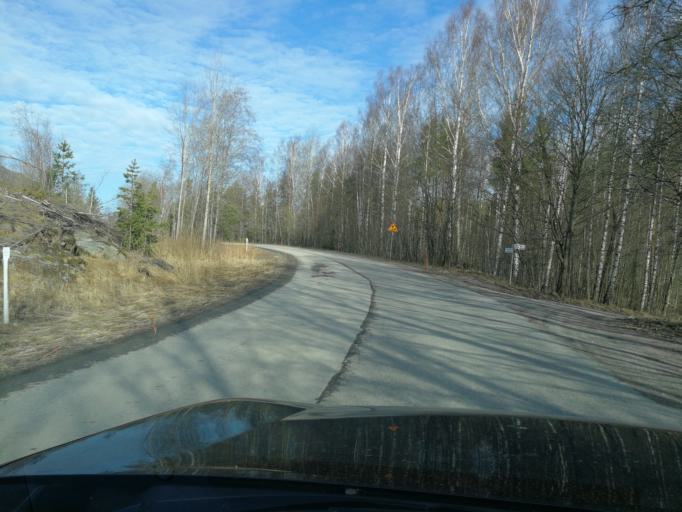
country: FI
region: Uusimaa
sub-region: Helsinki
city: Kirkkonummi
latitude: 60.0923
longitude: 24.3815
